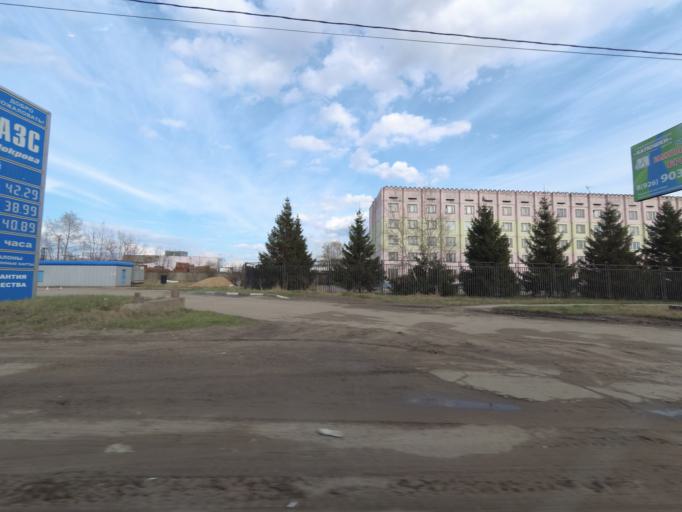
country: RU
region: Moskovskaya
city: Lobnya
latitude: 55.9856
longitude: 37.4176
